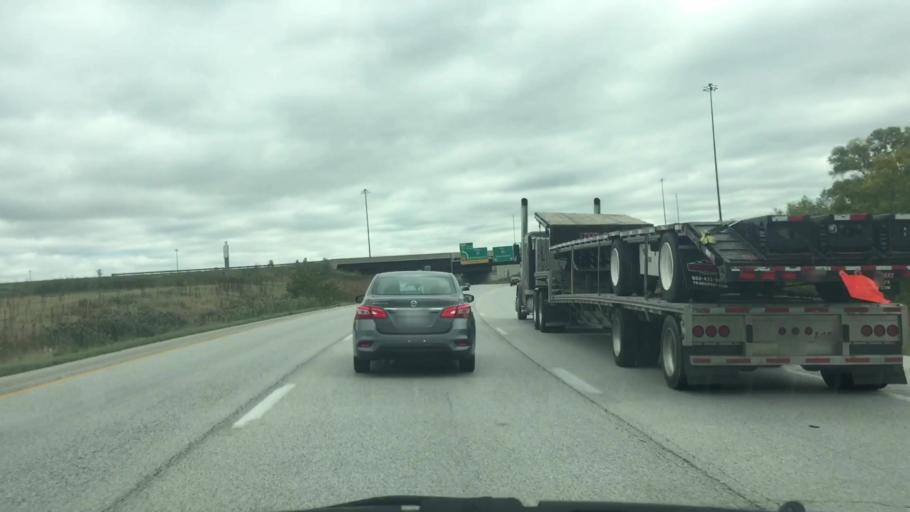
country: US
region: Iowa
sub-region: Polk County
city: Saylorville
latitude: 41.6511
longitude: -93.5801
